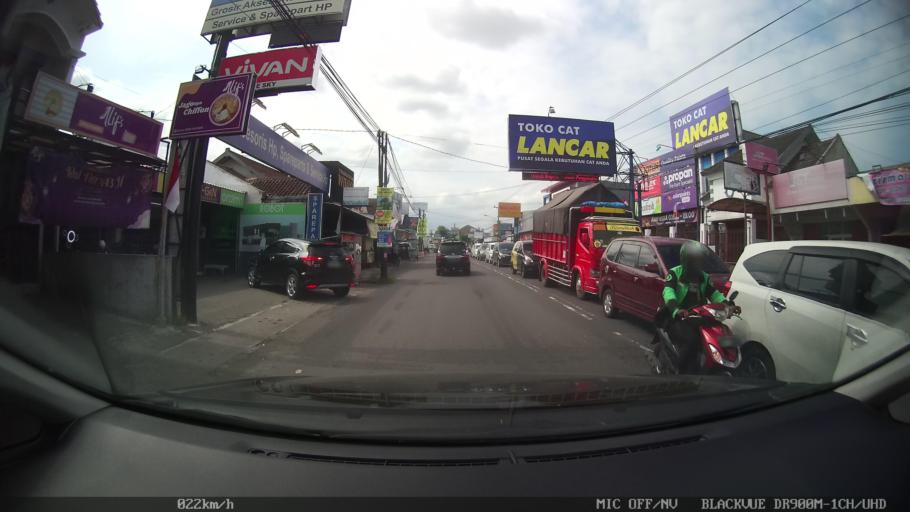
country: ID
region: Daerah Istimewa Yogyakarta
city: Depok
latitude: -7.7613
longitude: 110.4328
